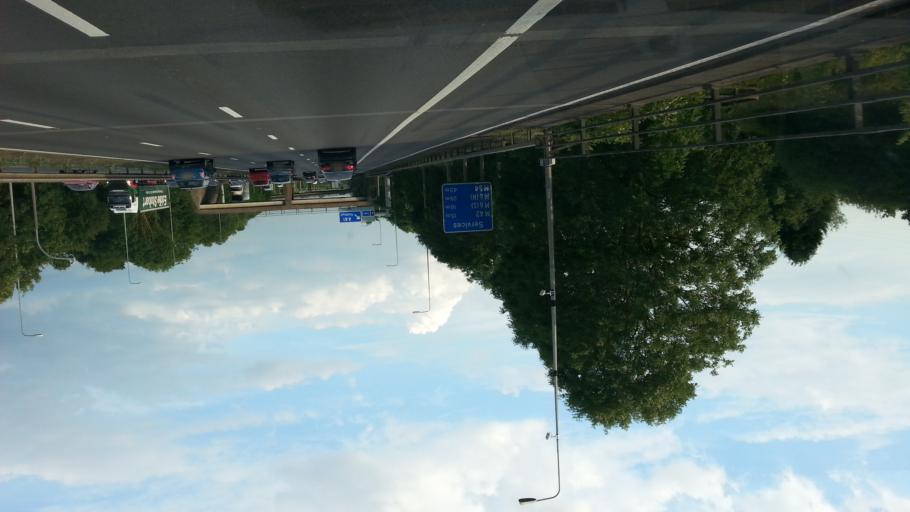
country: GB
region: England
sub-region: Solihull
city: Solihull
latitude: 52.3907
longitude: -1.7740
